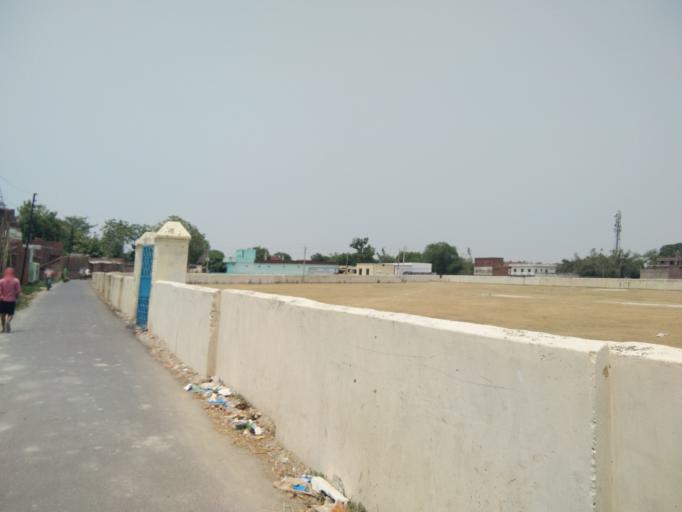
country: IN
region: Uttar Pradesh
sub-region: Ghazipur
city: Zamania
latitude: 25.4404
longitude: 83.6846
